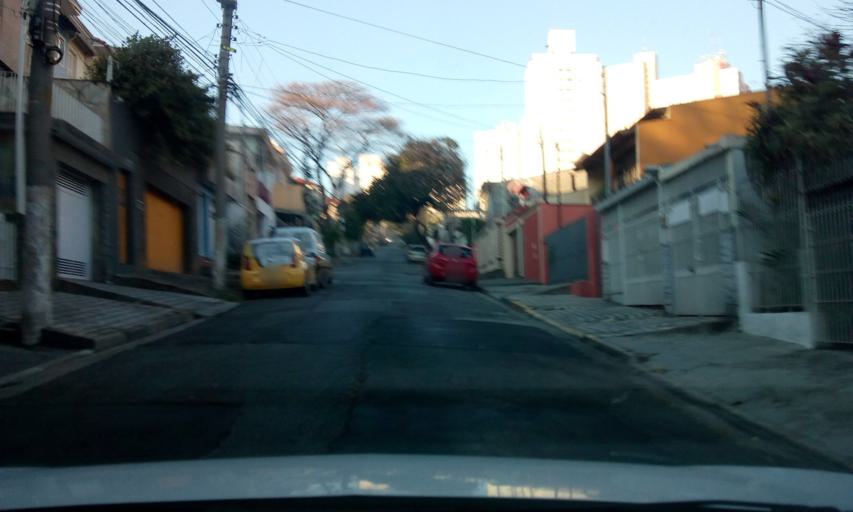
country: BR
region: Sao Paulo
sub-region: Sao Paulo
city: Sao Paulo
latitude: -23.5405
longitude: -46.6928
